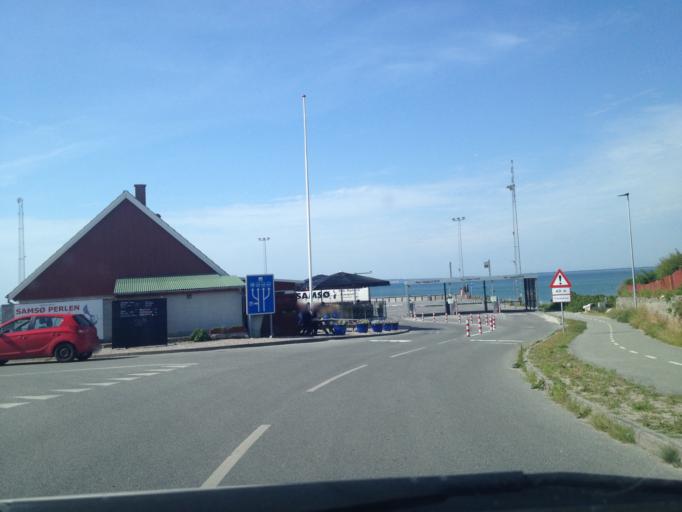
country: DK
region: Central Jutland
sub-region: Samso Kommune
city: Tranebjerg
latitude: 55.8629
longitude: 10.5499
